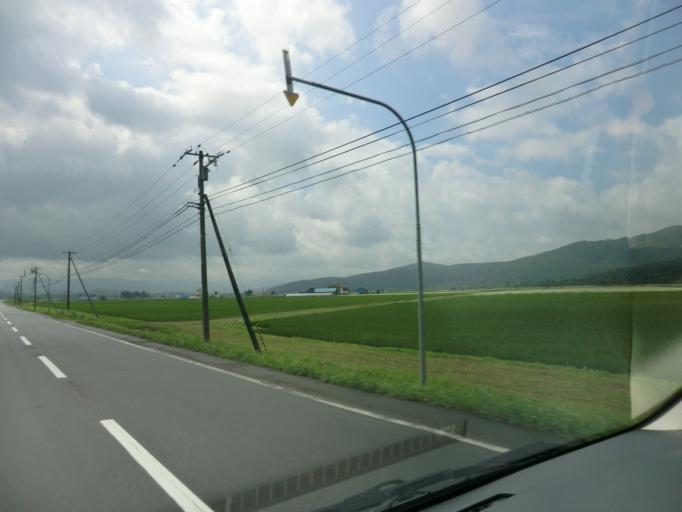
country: JP
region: Hokkaido
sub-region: Asahikawa-shi
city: Asahikawa
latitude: 44.0505
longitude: 142.1448
